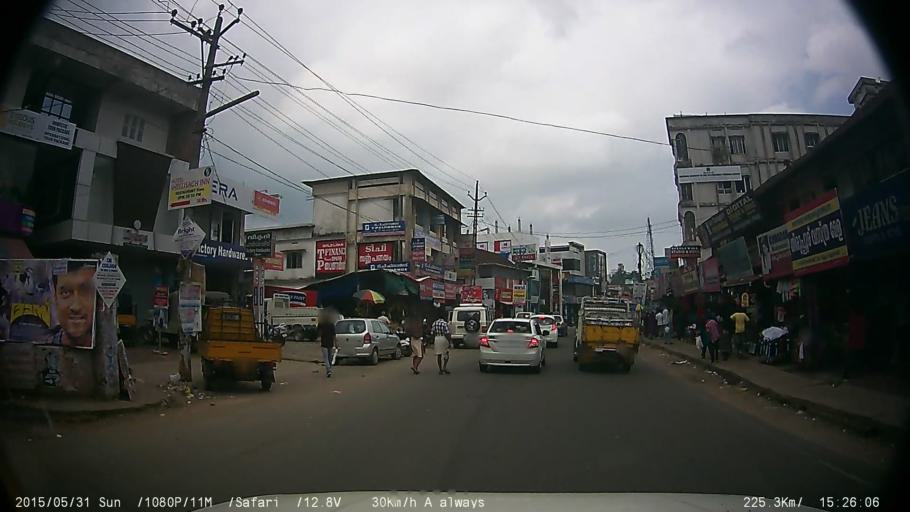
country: IN
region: Kerala
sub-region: Wayanad
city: Panamaram
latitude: 11.6632
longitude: 76.2557
